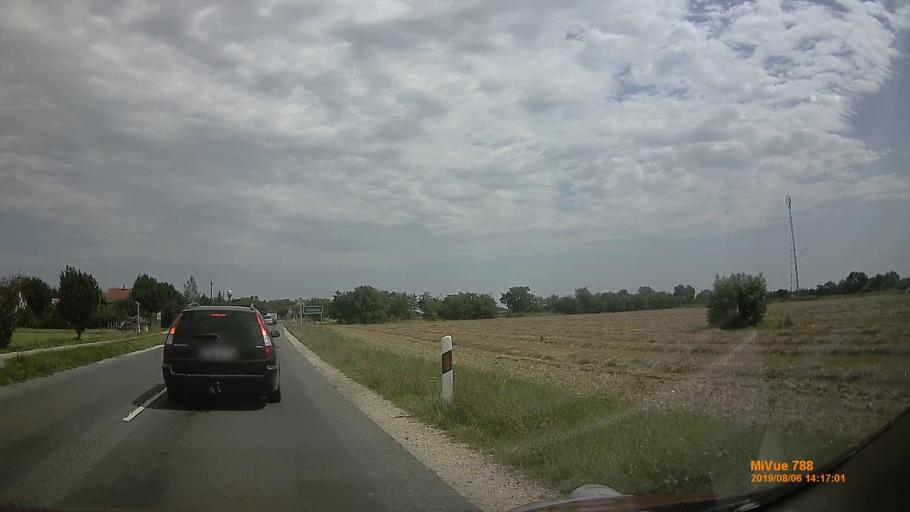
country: HU
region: Vas
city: Taplanszentkereszt
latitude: 47.1888
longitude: 16.7283
